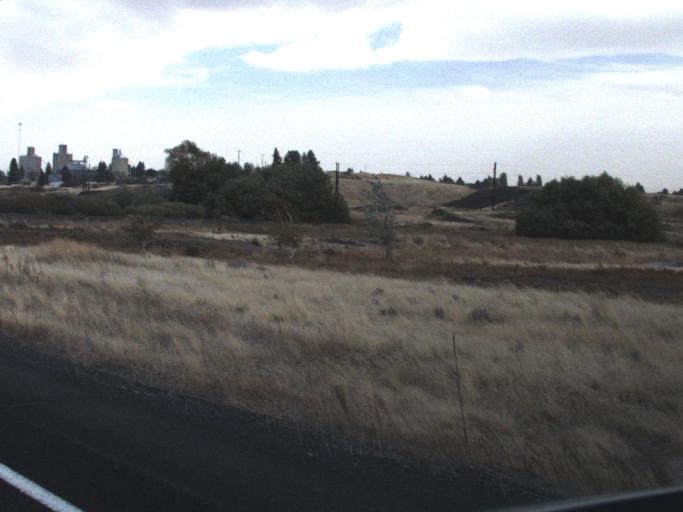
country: US
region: Washington
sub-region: Lincoln County
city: Davenport
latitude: 47.4776
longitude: -118.2691
